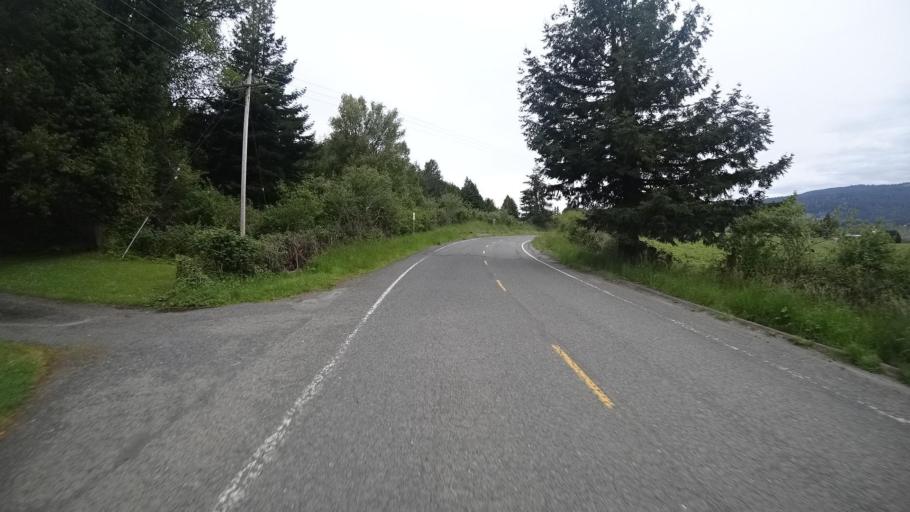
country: US
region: California
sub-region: Humboldt County
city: Blue Lake
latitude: 40.8578
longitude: -123.9953
